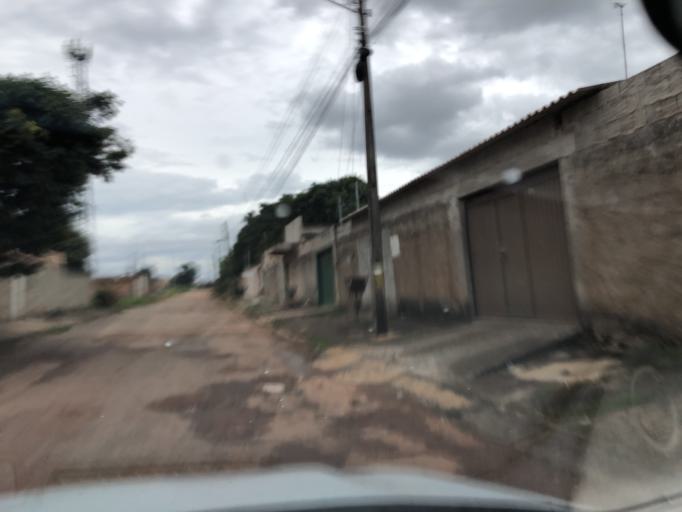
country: BR
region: Goias
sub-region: Luziania
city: Luziania
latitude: -16.1512
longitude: -47.9419
